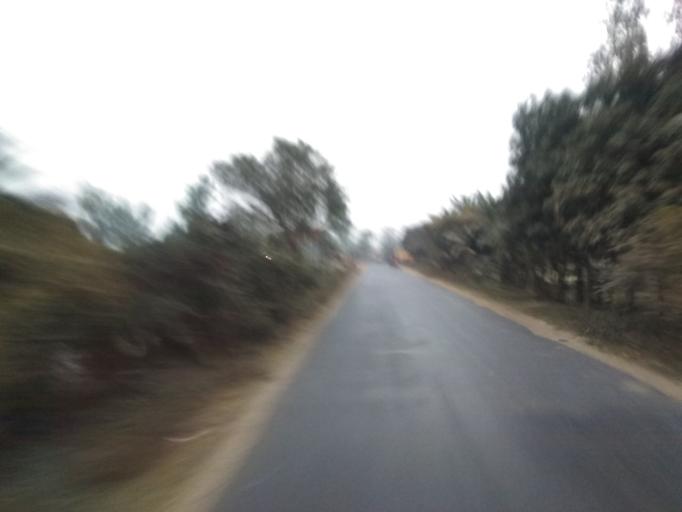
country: BD
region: Rajshahi
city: Bogra
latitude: 24.7381
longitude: 89.3307
